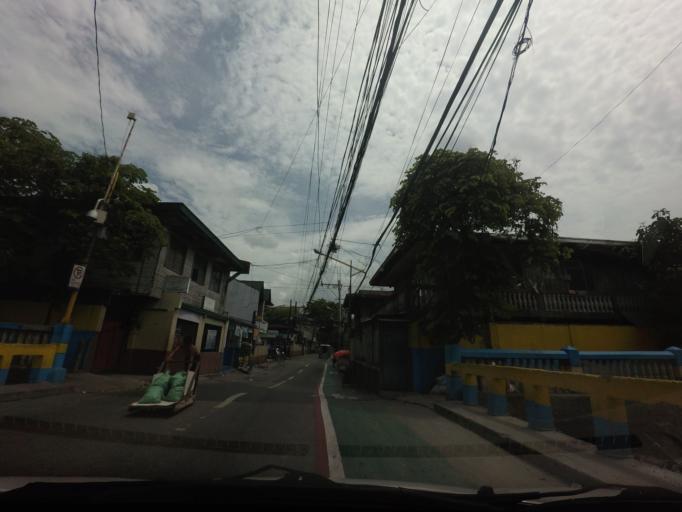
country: PH
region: Calabarzon
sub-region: Province of Rizal
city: Pateros
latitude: 14.5652
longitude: 121.0802
